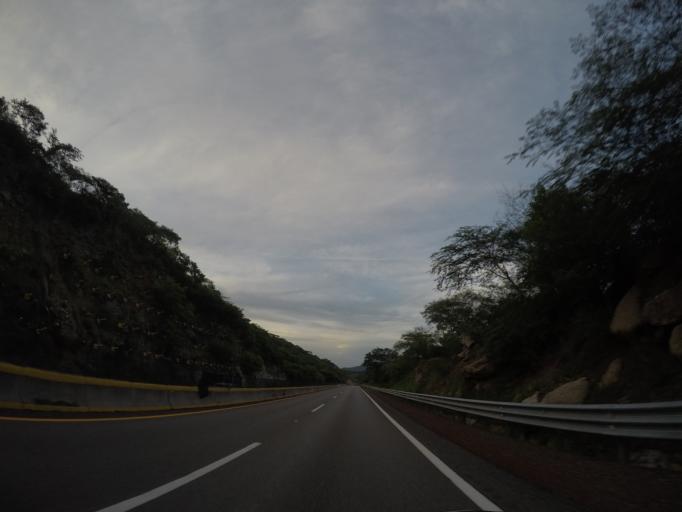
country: MX
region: Guerrero
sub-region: Huitzuco de los Figueroa
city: Ciudad de Huitzuco
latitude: 18.3400
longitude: -99.1899
